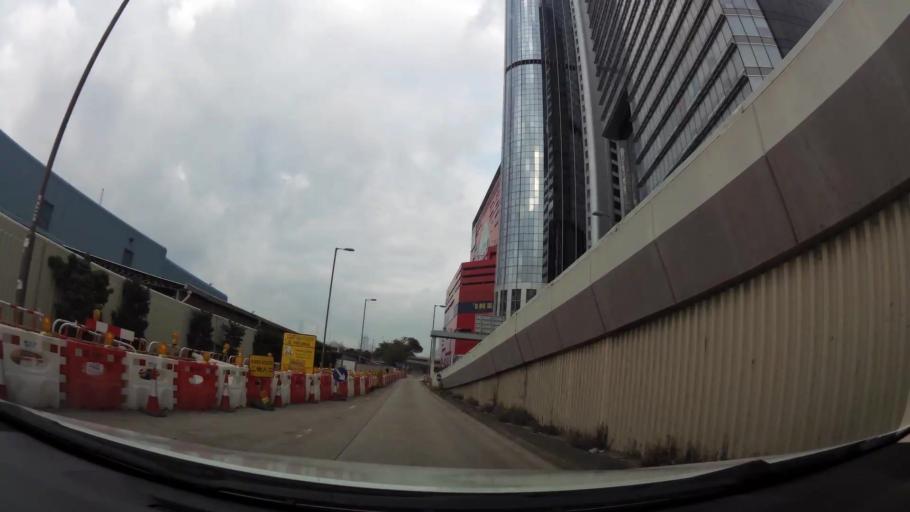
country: HK
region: Kowloon City
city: Kowloon
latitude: 22.3193
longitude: 114.2107
